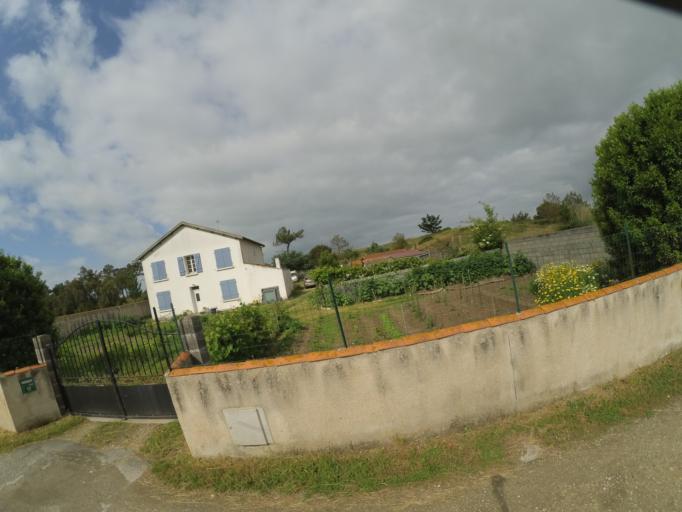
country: FR
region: Poitou-Charentes
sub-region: Departement de la Charente-Maritime
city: Aytre
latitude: 46.1187
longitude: -1.1231
